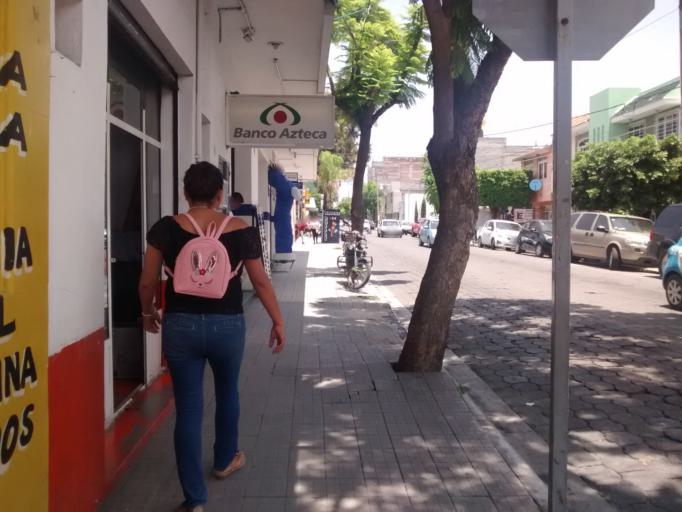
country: MX
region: Puebla
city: Tehuacan
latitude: 18.4668
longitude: -97.3914
